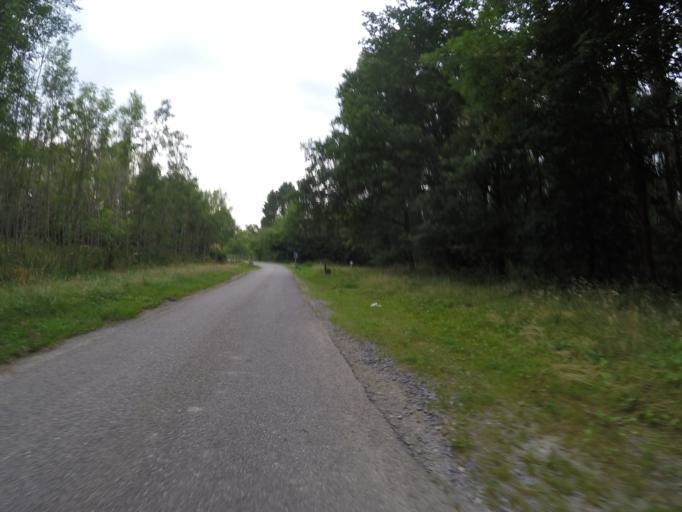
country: BE
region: Wallonia
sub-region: Province de Namur
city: Assesse
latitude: 50.3164
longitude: 5.0380
